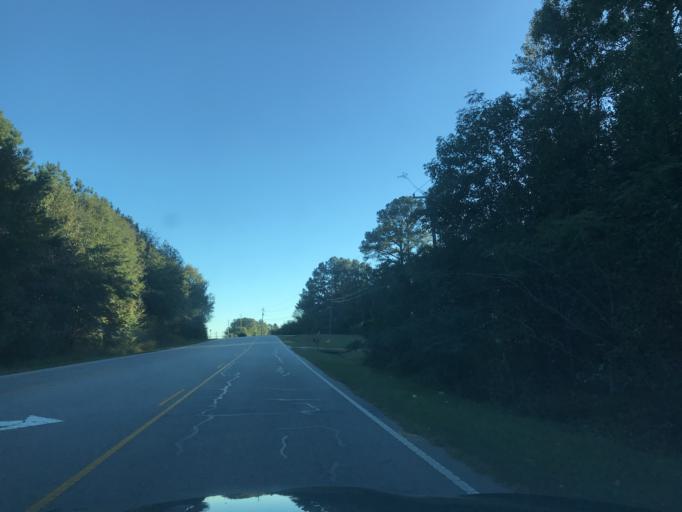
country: US
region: North Carolina
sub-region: Wake County
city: Garner
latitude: 35.7498
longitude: -78.5859
